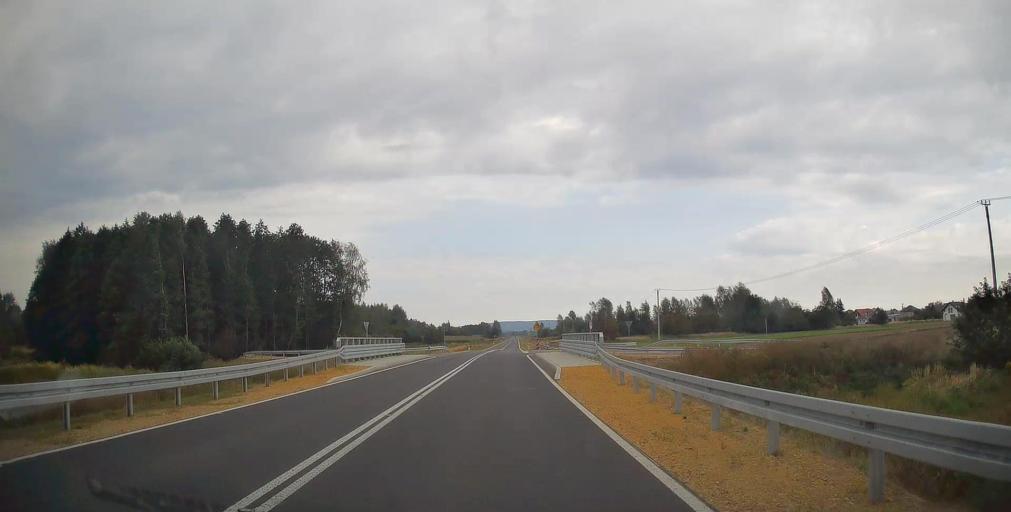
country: PL
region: Lesser Poland Voivodeship
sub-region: Powiat oswiecimski
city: Zator
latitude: 50.0057
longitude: 19.4234
